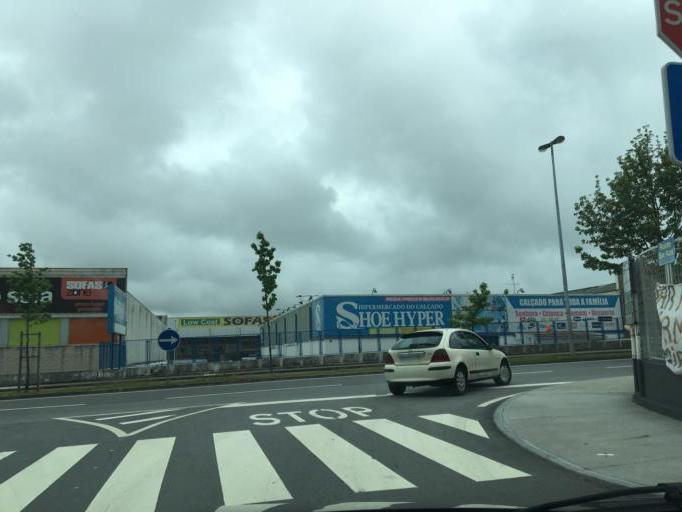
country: PT
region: Porto
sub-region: Maia
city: Maia
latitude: 41.2457
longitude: -8.6267
